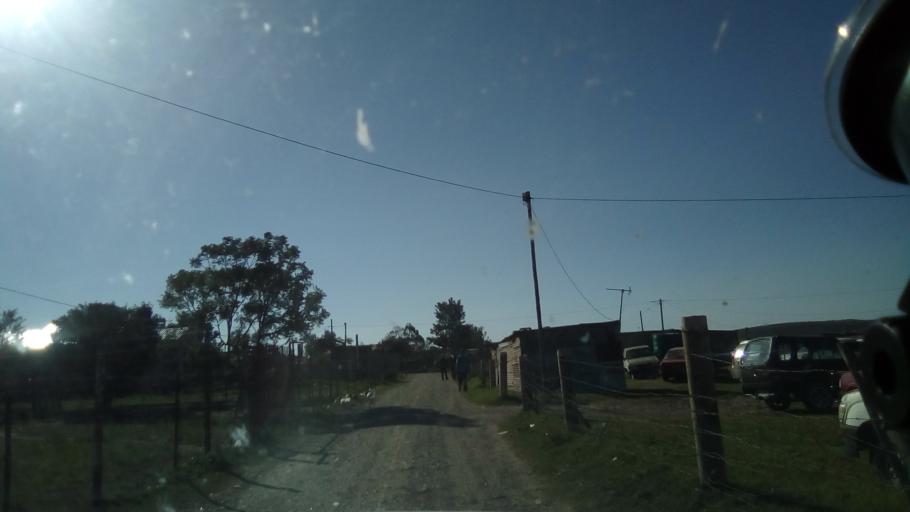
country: ZA
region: Eastern Cape
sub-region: Buffalo City Metropolitan Municipality
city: Bhisho
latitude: -32.8274
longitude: 27.3735
